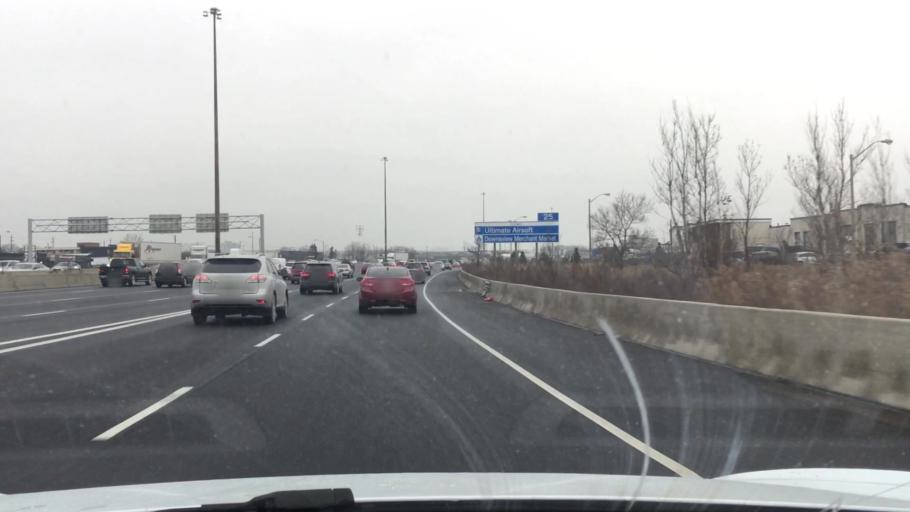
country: CA
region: Ontario
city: Etobicoke
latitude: 43.7202
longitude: -79.5212
